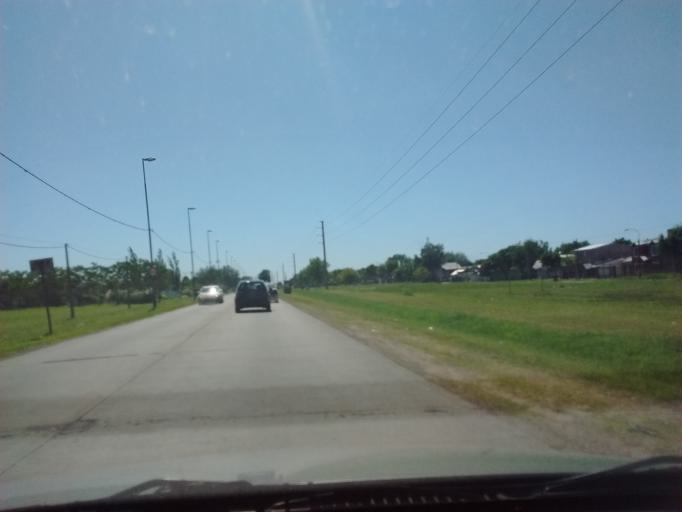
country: AR
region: Santa Fe
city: Granadero Baigorria
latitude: -32.9085
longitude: -60.7346
